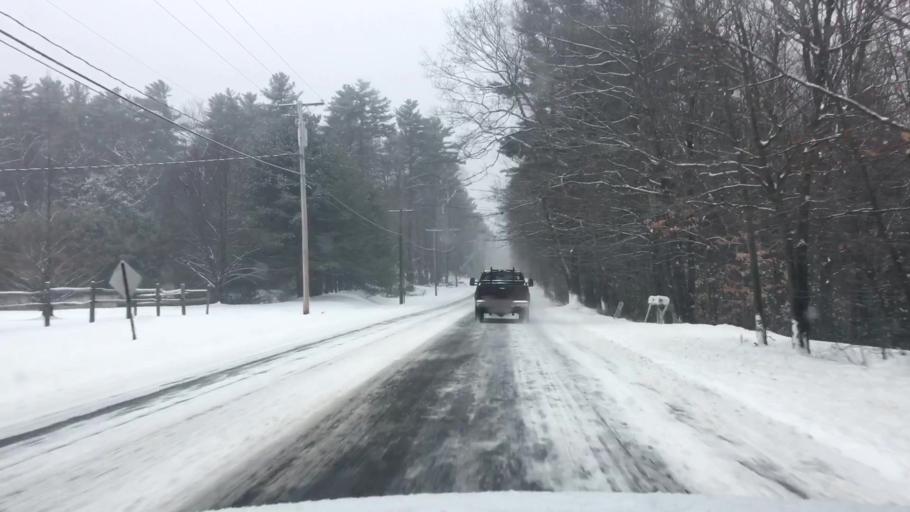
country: US
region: Maine
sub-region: Cumberland County
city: Cumberland Center
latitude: 43.8276
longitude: -70.3175
